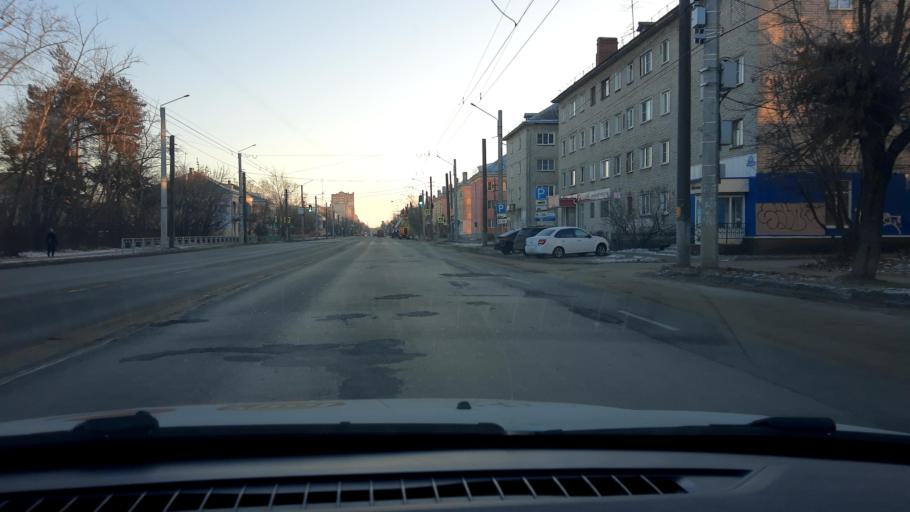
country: RU
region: Nizjnij Novgorod
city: Dzerzhinsk
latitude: 56.2496
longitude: 43.4509
